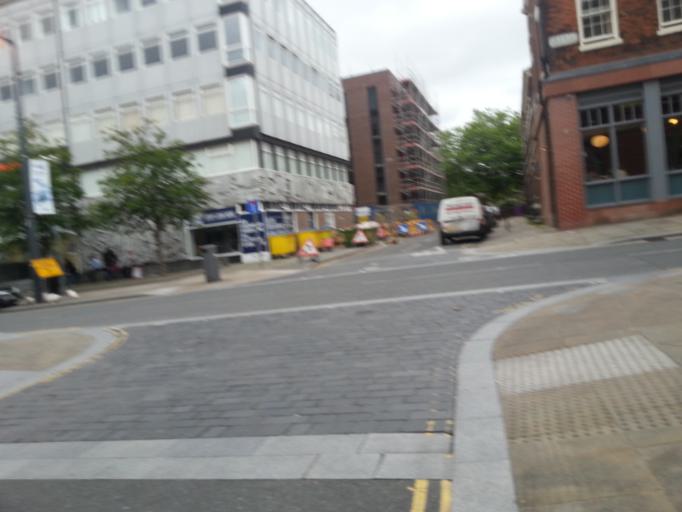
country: GB
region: England
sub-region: Liverpool
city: Liverpool
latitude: 53.4007
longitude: -2.9711
